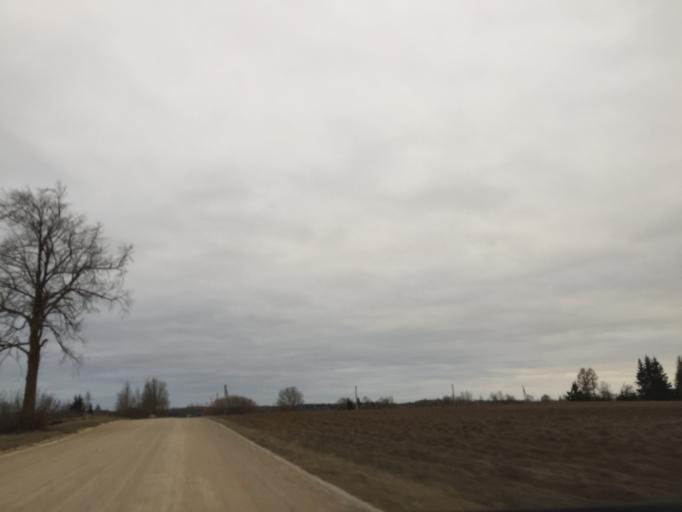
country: LT
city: Zagare
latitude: 56.2754
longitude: 23.2613
